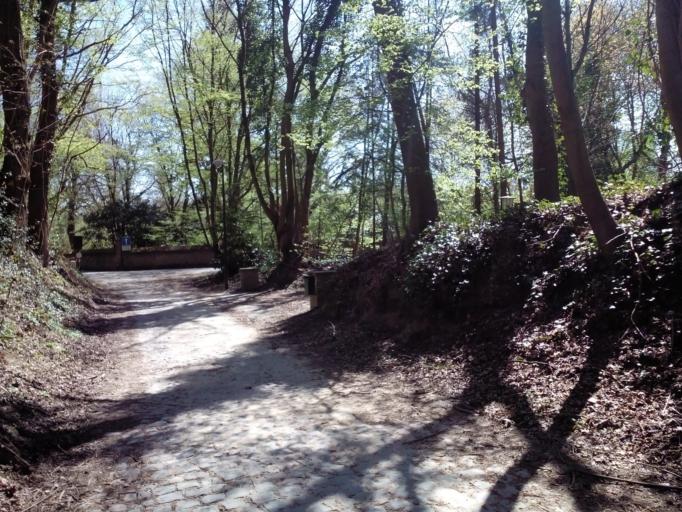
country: BE
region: Flanders
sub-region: Provincie Vlaams-Brabant
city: Tervuren
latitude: 50.8330
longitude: 4.5433
